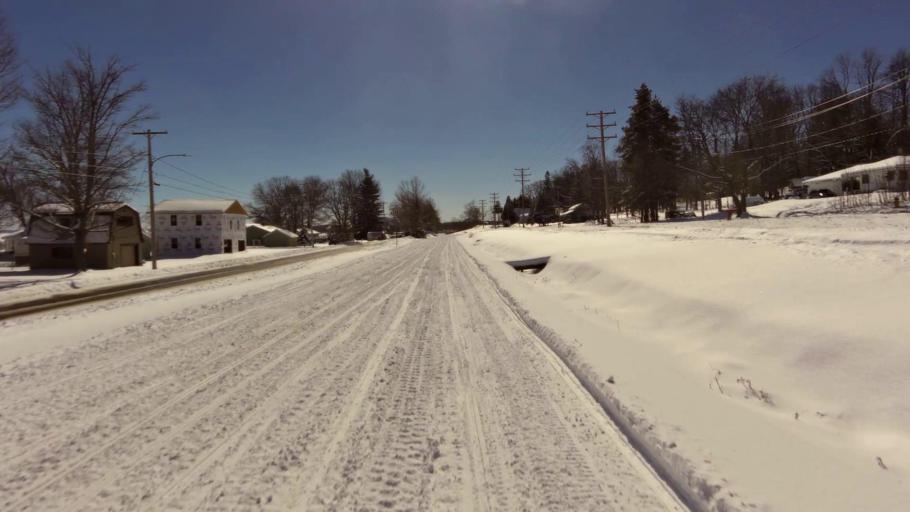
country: US
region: New York
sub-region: Chautauqua County
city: Mayville
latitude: 42.2525
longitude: -79.4940
